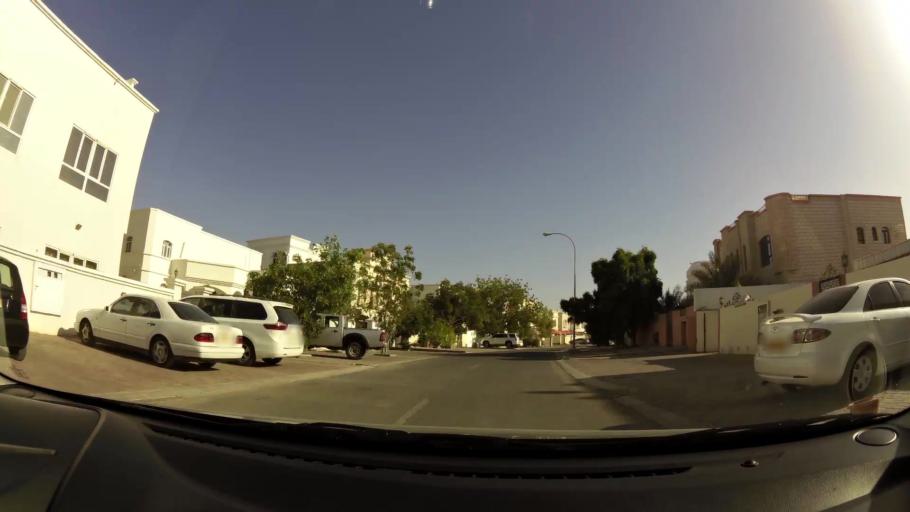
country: OM
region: Muhafazat Masqat
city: As Sib al Jadidah
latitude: 23.5995
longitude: 58.2163
